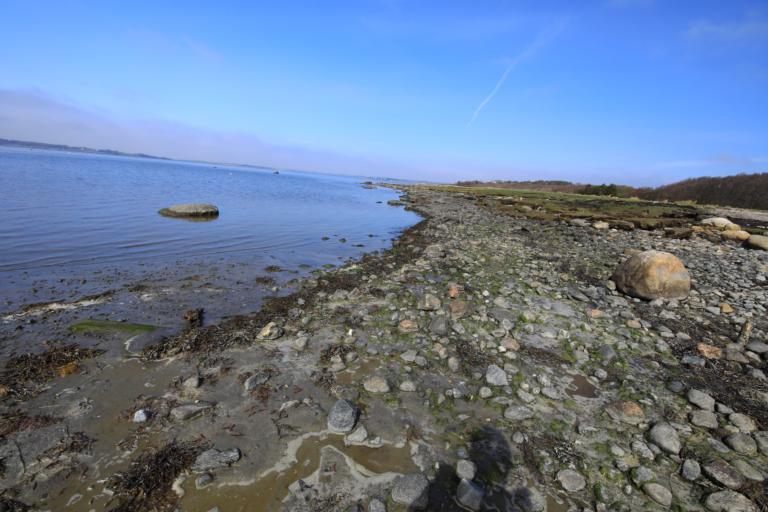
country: SE
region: Halland
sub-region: Kungsbacka Kommun
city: Frillesas
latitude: 57.2851
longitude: 12.1639
